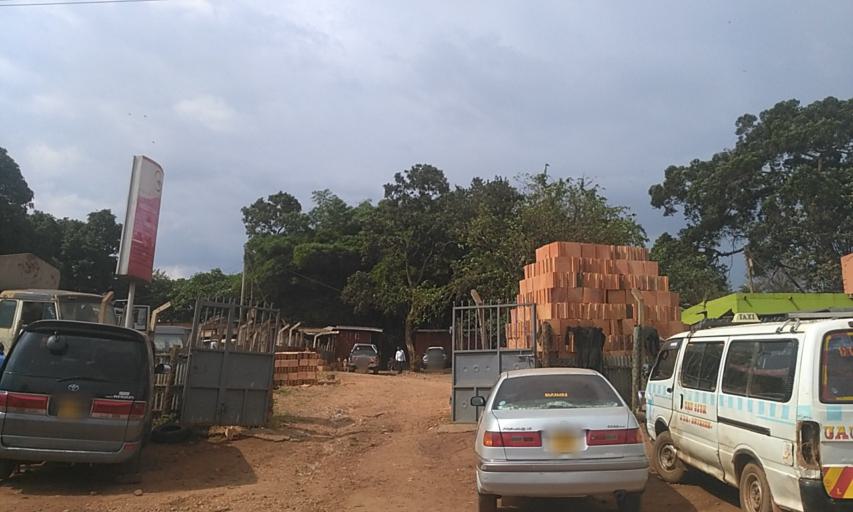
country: UG
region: Central Region
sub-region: Kampala District
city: Kampala
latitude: 0.2945
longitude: 32.5534
